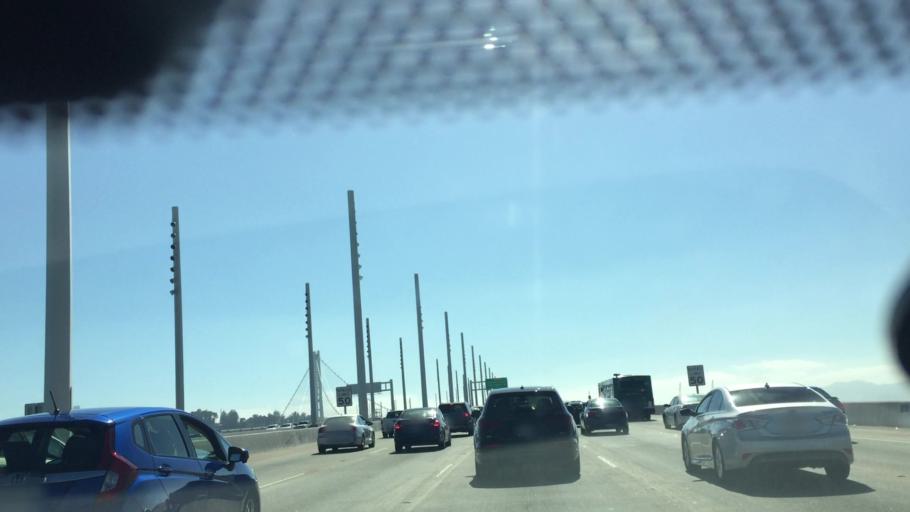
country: US
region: California
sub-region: Alameda County
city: Emeryville
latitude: 37.8209
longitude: -122.3452
